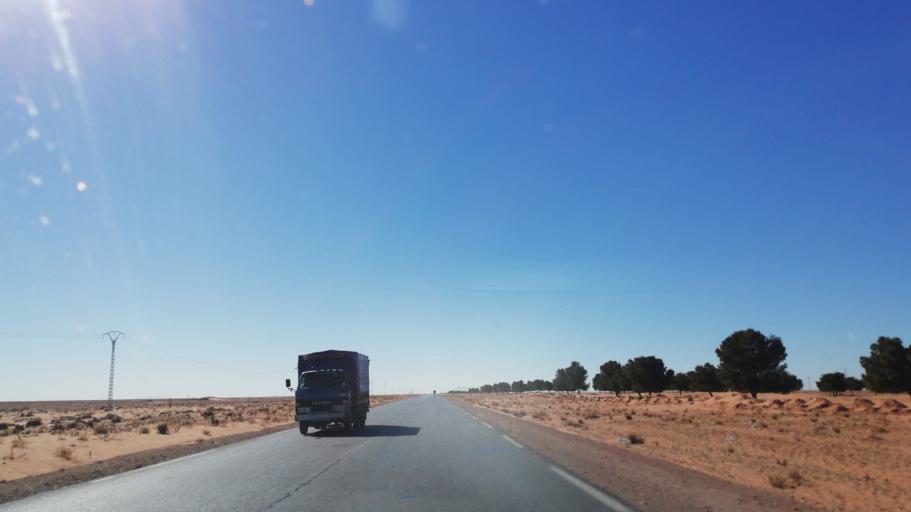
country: DZ
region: Wilaya de Naama
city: Naama
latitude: 33.9734
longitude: 0.0229
